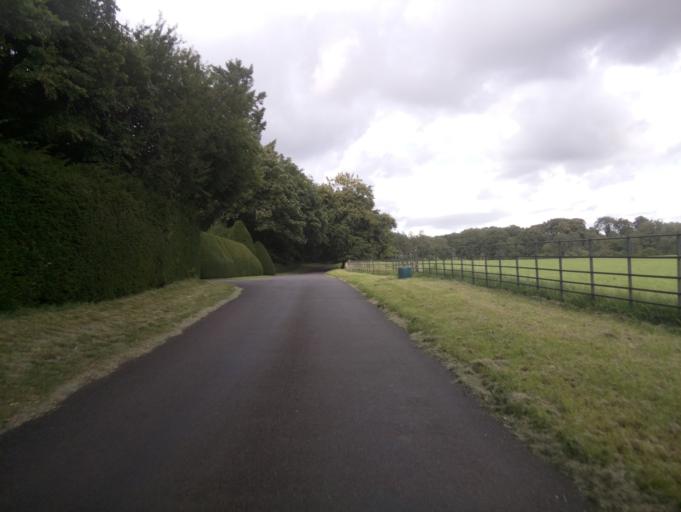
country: GB
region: England
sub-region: Gloucestershire
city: Coates
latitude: 51.7541
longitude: -2.0666
